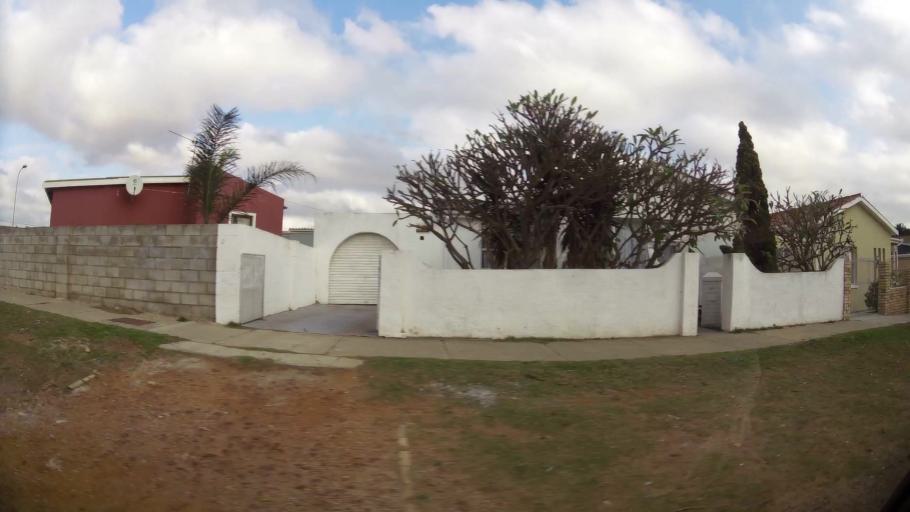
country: ZA
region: Eastern Cape
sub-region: Nelson Mandela Bay Metropolitan Municipality
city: Port Elizabeth
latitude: -33.9142
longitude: 25.5499
